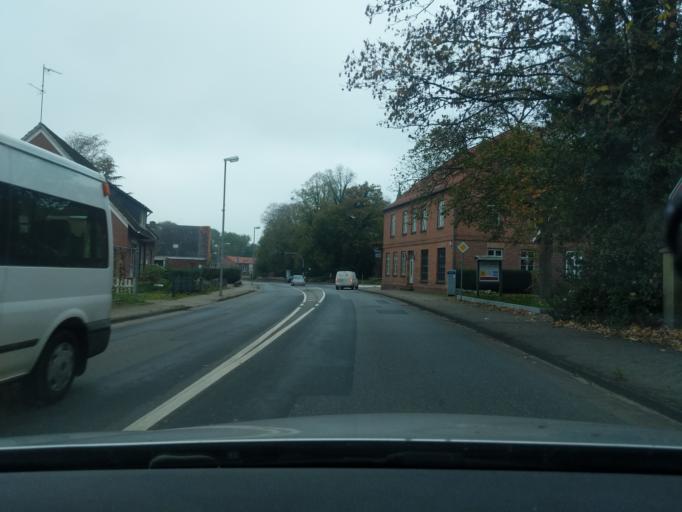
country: DE
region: Lower Saxony
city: Himmelpforten
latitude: 53.6138
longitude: 9.3062
